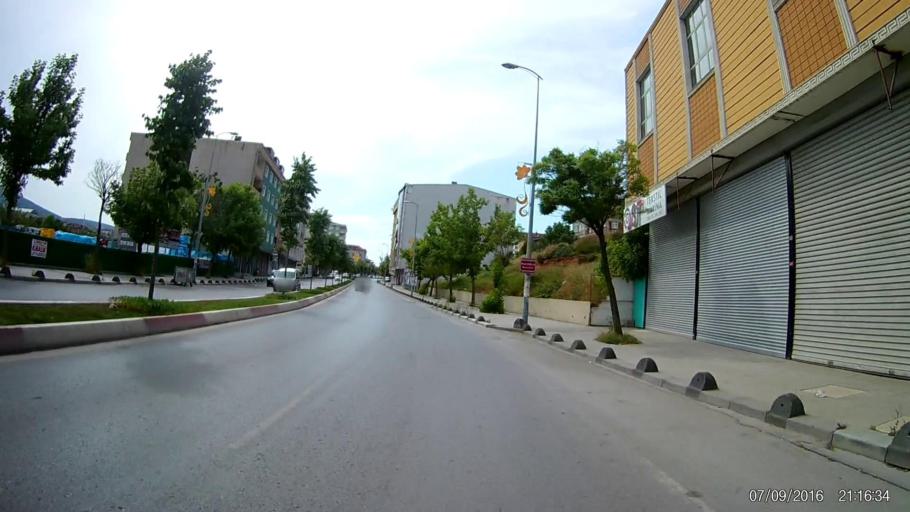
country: TR
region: Istanbul
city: Sultanbeyli
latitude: 40.9623
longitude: 29.2893
